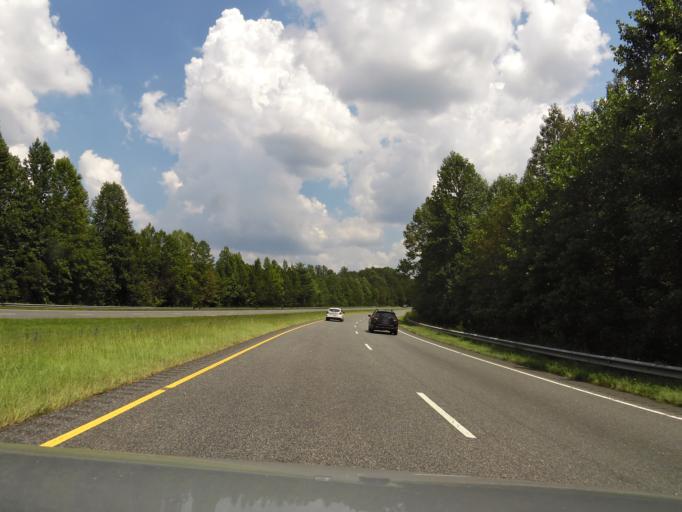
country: US
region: North Carolina
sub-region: Polk County
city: Columbus
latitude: 35.2780
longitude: -82.1291
